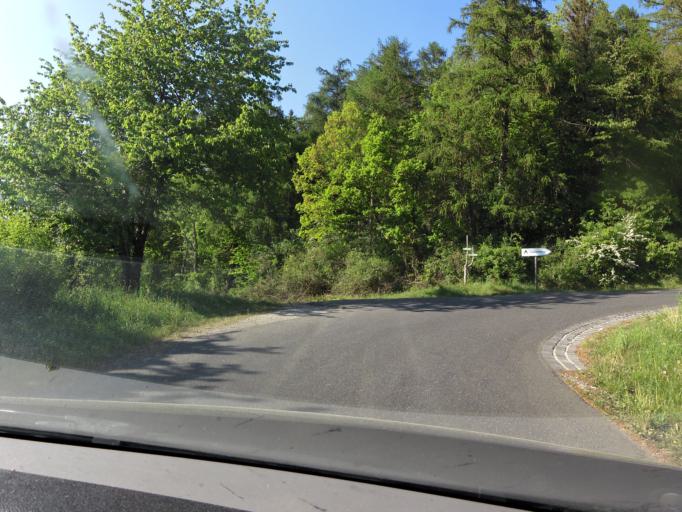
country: DE
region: Thuringia
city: Lauterbach
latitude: 51.0759
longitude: 10.3630
